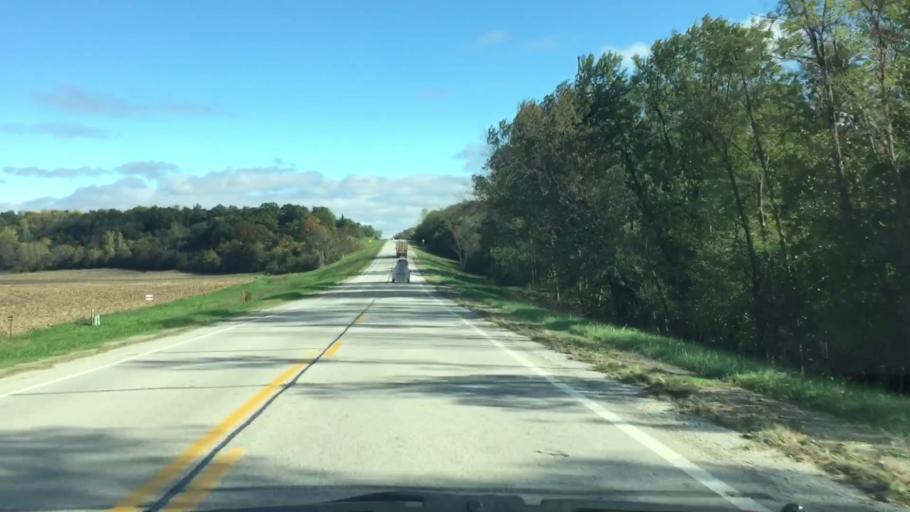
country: US
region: Iowa
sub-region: Decatur County
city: Leon
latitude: 40.6531
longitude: -93.7999
